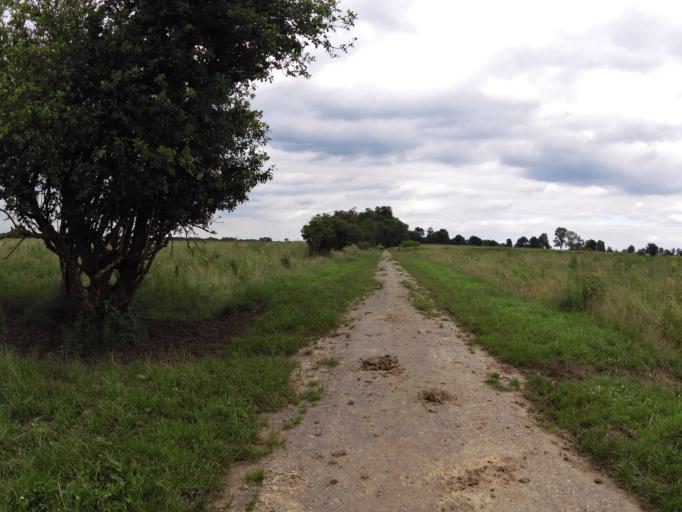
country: NL
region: North Brabant
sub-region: Gemeente Landerd
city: Reek
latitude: 51.7678
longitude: 5.6836
